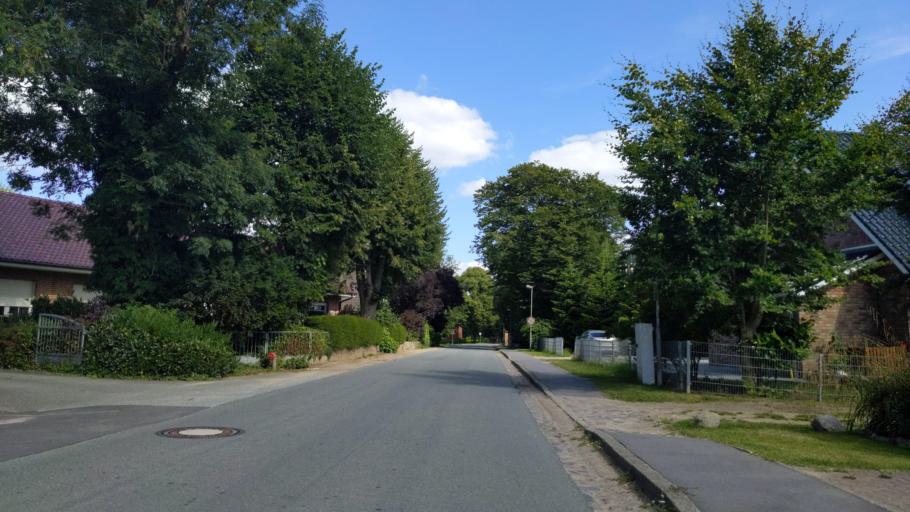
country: DE
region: Schleswig-Holstein
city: Stockelsdorf
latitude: 53.9150
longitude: 10.6048
